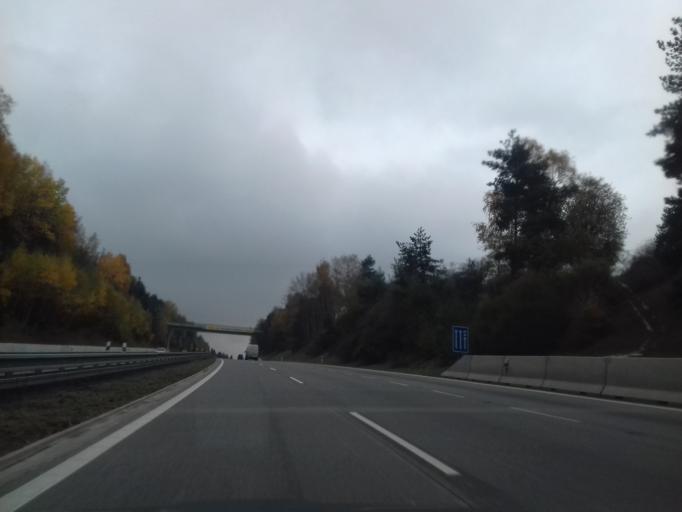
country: CZ
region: Vysocina
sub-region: Okres Pelhrimov
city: Zeliv
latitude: 49.5999
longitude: 15.1937
